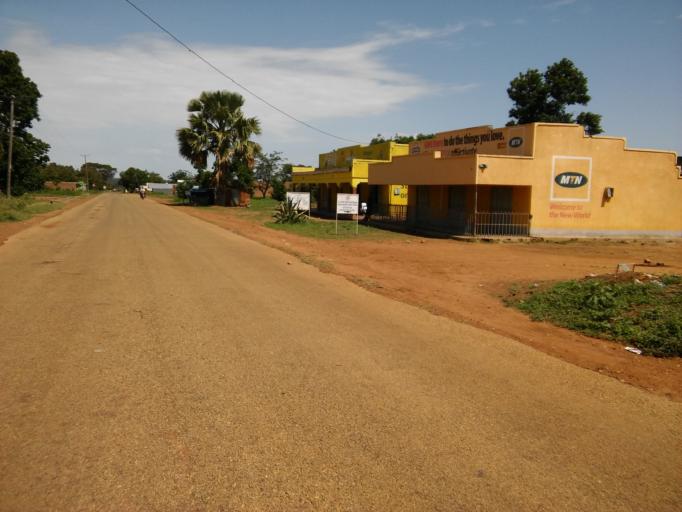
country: UG
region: Eastern Region
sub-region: Kumi District
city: Kumi
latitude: 1.4866
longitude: 33.9271
